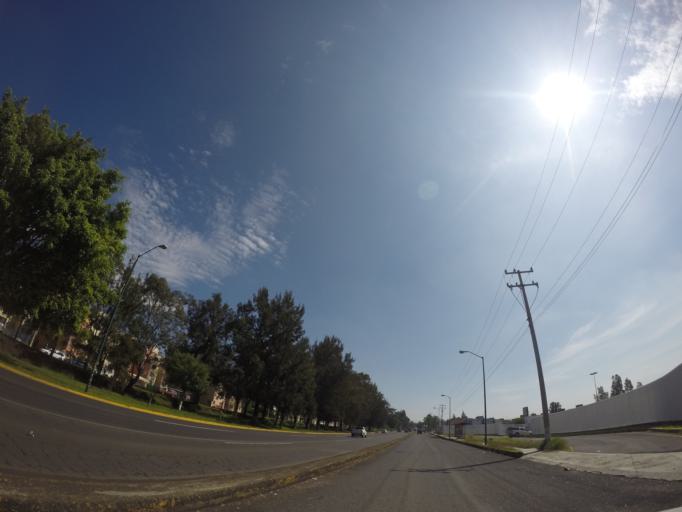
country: MX
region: Michoacan
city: Morelia
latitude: 19.7108
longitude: -101.2338
